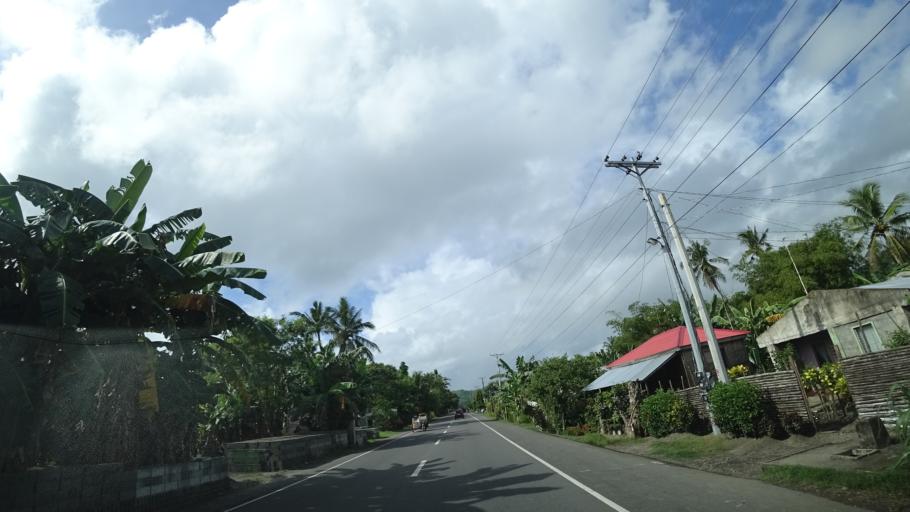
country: PH
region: Eastern Visayas
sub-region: Province of Leyte
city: San Roque
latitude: 11.0227
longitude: 125.0365
